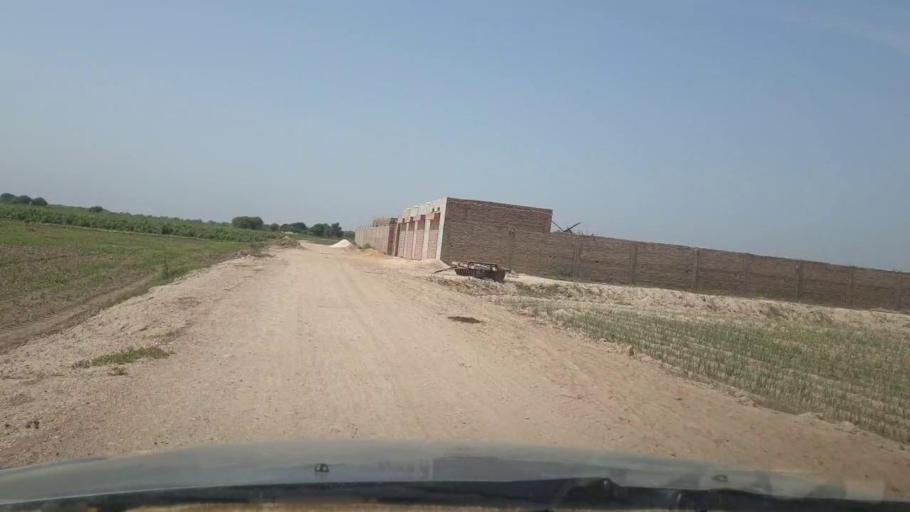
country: PK
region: Sindh
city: Chambar
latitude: 25.2592
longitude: 68.7548
